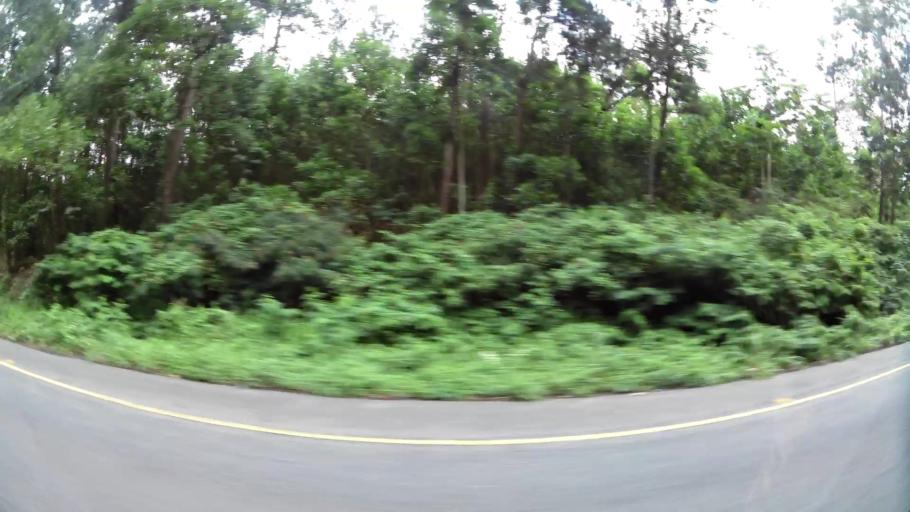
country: DO
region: Monsenor Nouel
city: Piedra Blanca
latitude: 18.8080
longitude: -70.2795
